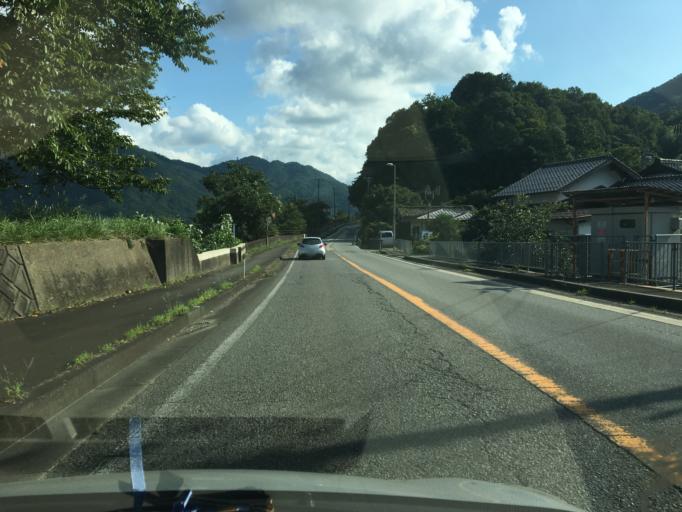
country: JP
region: Hyogo
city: Toyooka
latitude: 35.4340
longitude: 134.7889
